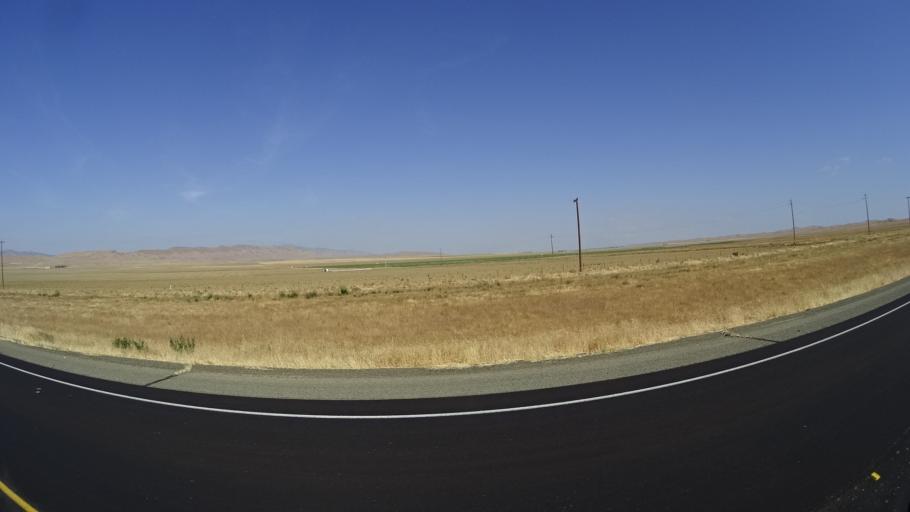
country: US
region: California
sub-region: Kings County
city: Kettleman City
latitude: 35.9191
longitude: -120.0274
